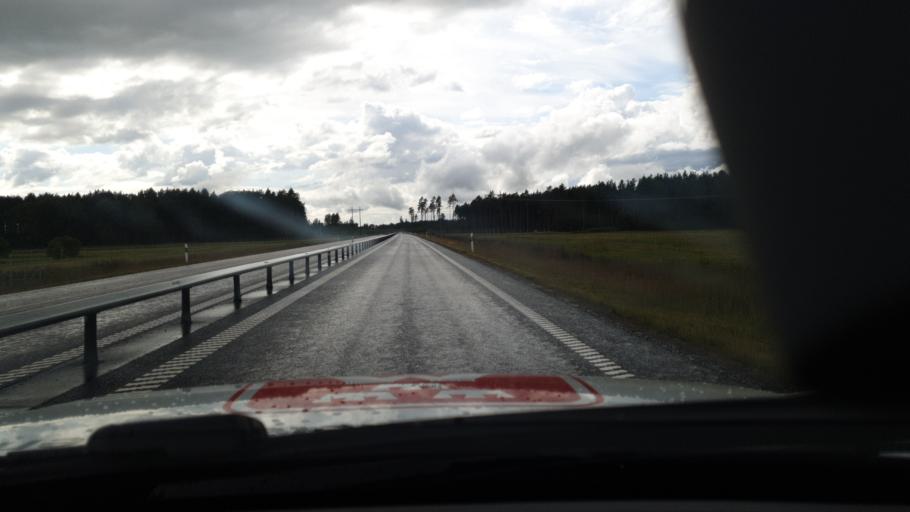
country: SE
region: Vaestra Goetaland
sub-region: Lidkopings Kommun
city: Vinninga
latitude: 58.4789
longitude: 13.2237
